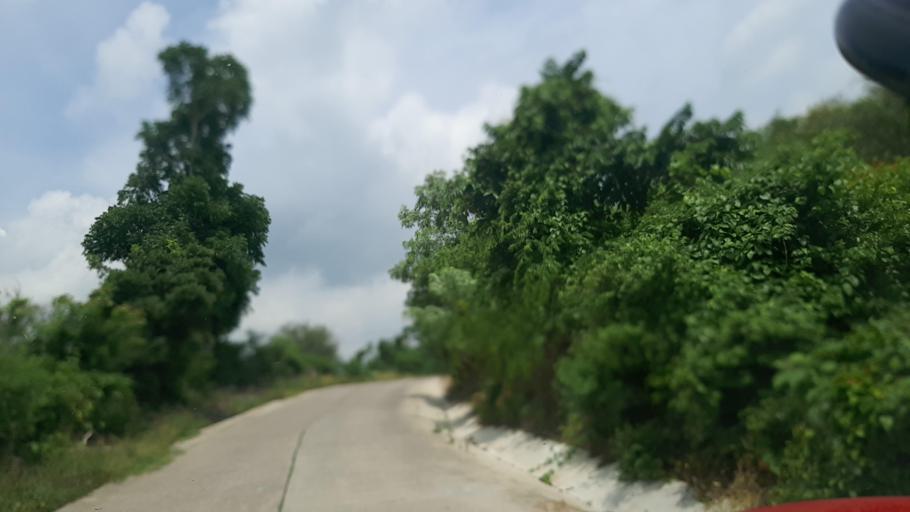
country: MX
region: Veracruz
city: Gutierrez Zamora
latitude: 20.4444
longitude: -97.1704
